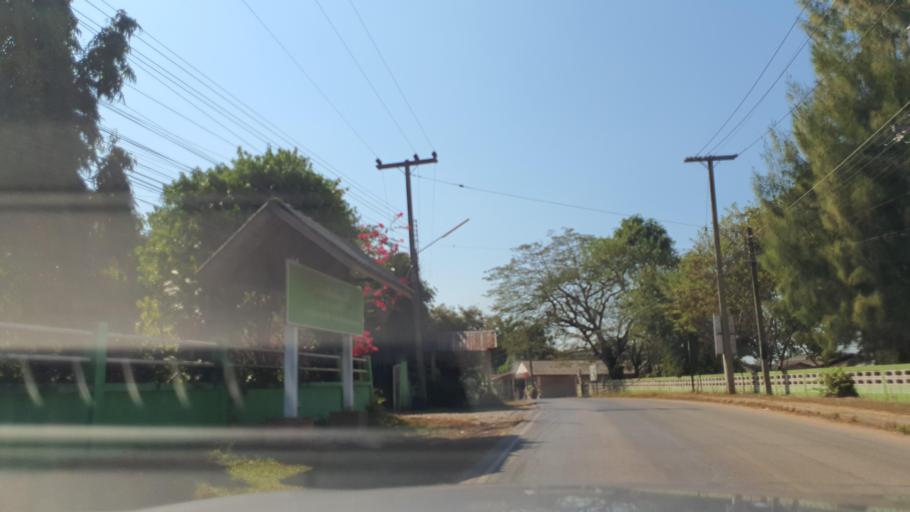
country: TH
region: Nan
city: Pua
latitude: 19.1364
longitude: 100.9321
